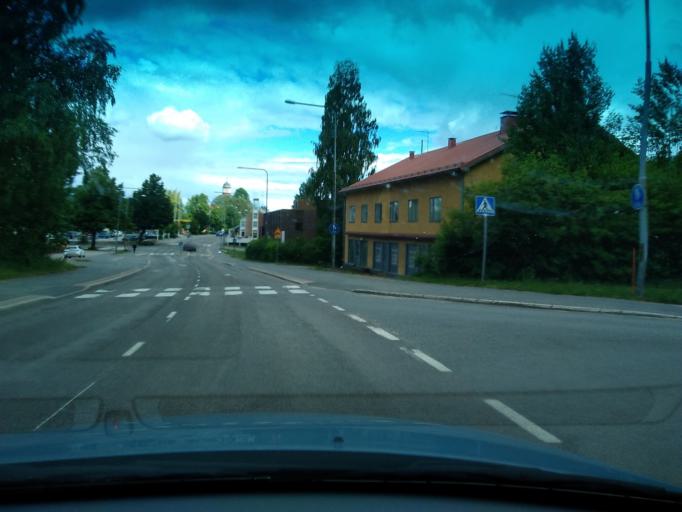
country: FI
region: Central Finland
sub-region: Saarijaervi-Viitasaari
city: Saarijaervi
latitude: 62.7044
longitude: 25.2581
